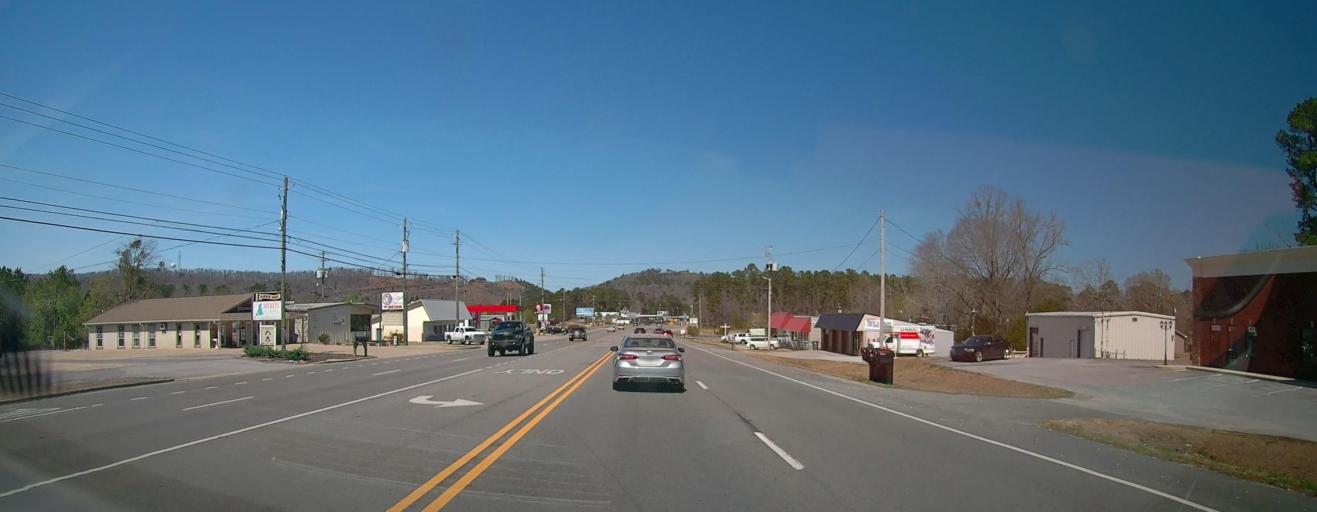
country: US
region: Alabama
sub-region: Etowah County
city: Southside
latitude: 33.9295
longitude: -86.0238
